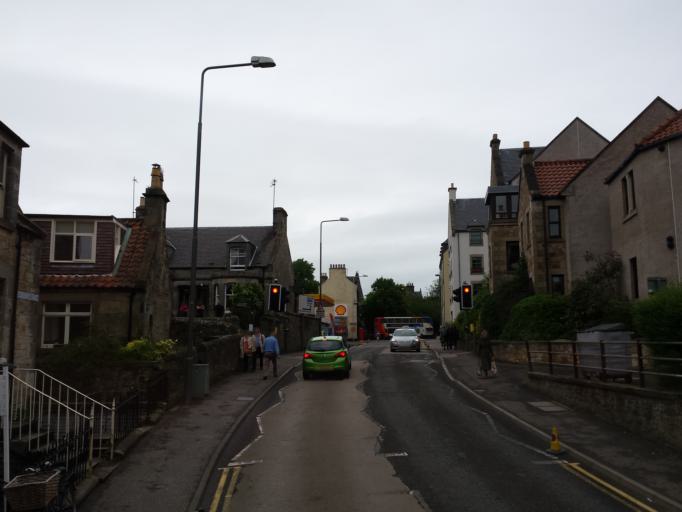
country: GB
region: Scotland
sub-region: Fife
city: Saint Andrews
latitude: 56.3376
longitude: -2.8009
